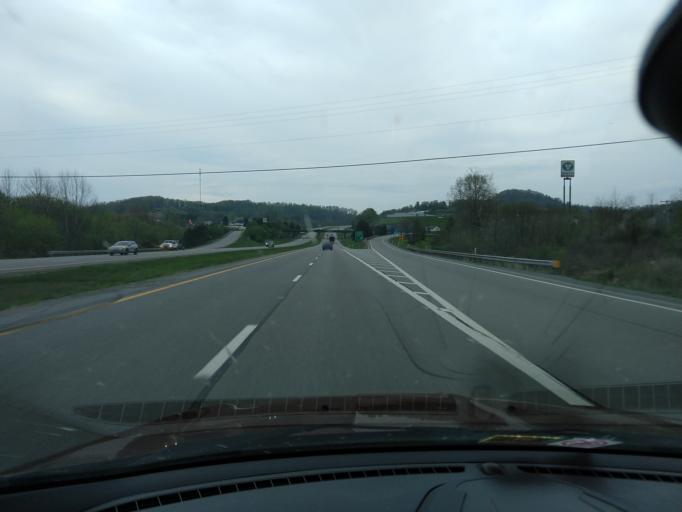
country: US
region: West Virginia
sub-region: Lewis County
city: Weston
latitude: 39.1005
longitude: -80.3920
